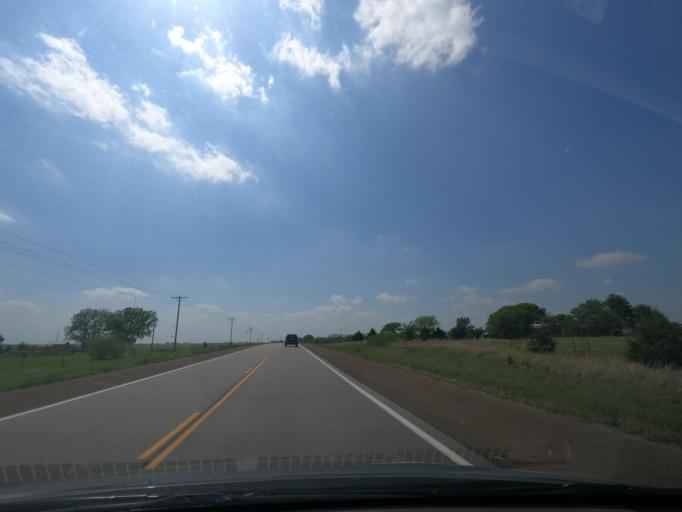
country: US
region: Kansas
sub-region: Butler County
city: El Dorado
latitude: 37.6795
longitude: -96.8237
